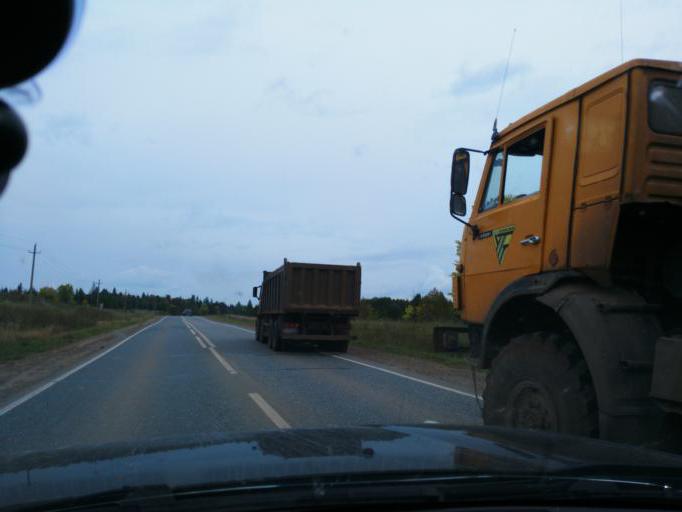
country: RU
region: Perm
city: Chernushka
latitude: 56.5061
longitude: 55.8753
